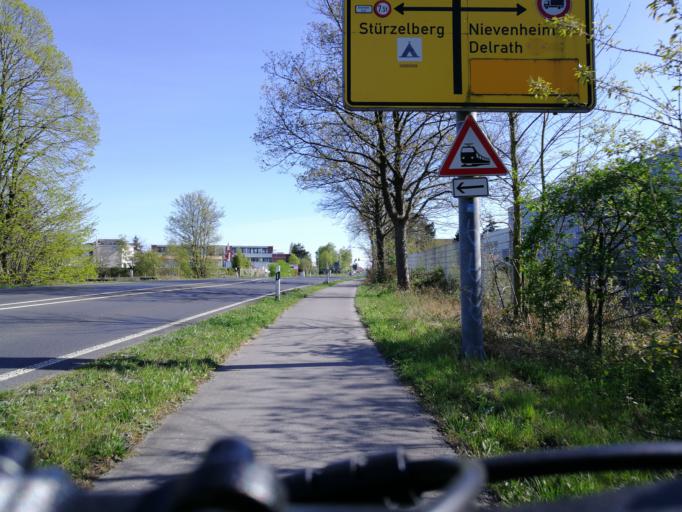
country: DE
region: North Rhine-Westphalia
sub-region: Regierungsbezirk Dusseldorf
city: Dormagen
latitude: 51.1374
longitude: 6.8007
